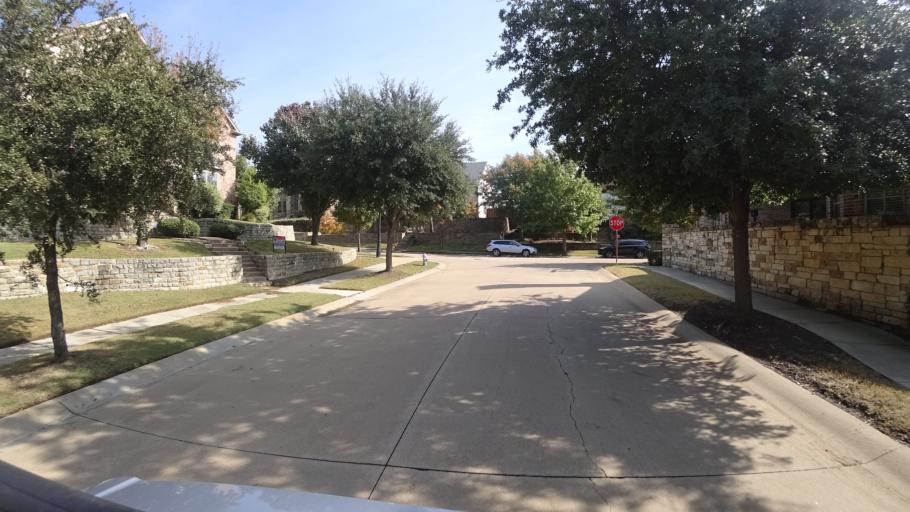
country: US
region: Texas
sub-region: Denton County
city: The Colony
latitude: 33.0346
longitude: -96.8948
